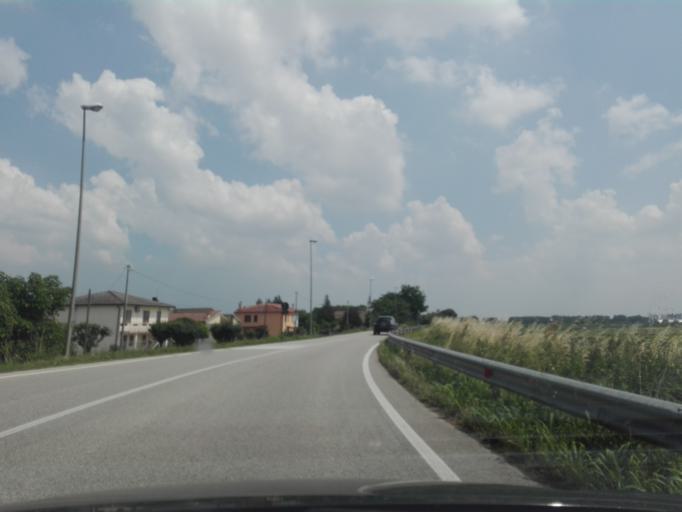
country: IT
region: Veneto
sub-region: Provincia di Rovigo
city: Adria
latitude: 45.0603
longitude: 12.0131
